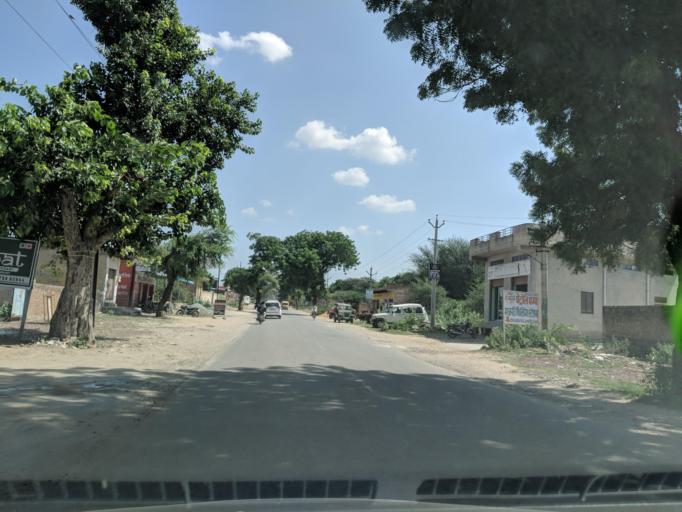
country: IN
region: Rajasthan
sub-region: Jhunjhunun
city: Jhunjhunun
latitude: 28.1364
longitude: 75.3867
